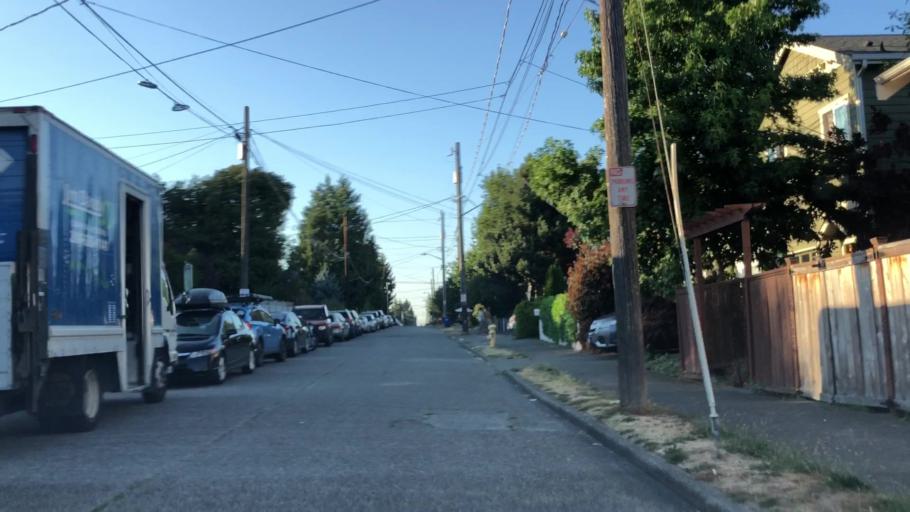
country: US
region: Washington
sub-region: King County
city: Seattle
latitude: 47.6453
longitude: -122.3833
